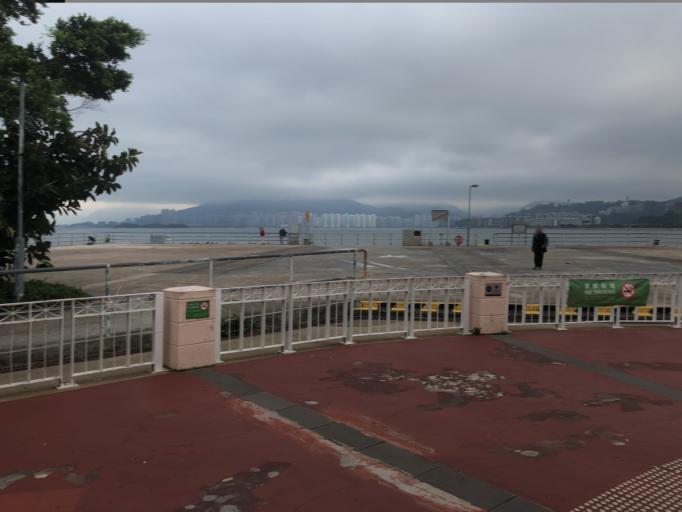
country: HK
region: Tai Po
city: Tai Po
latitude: 22.4512
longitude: 114.1928
